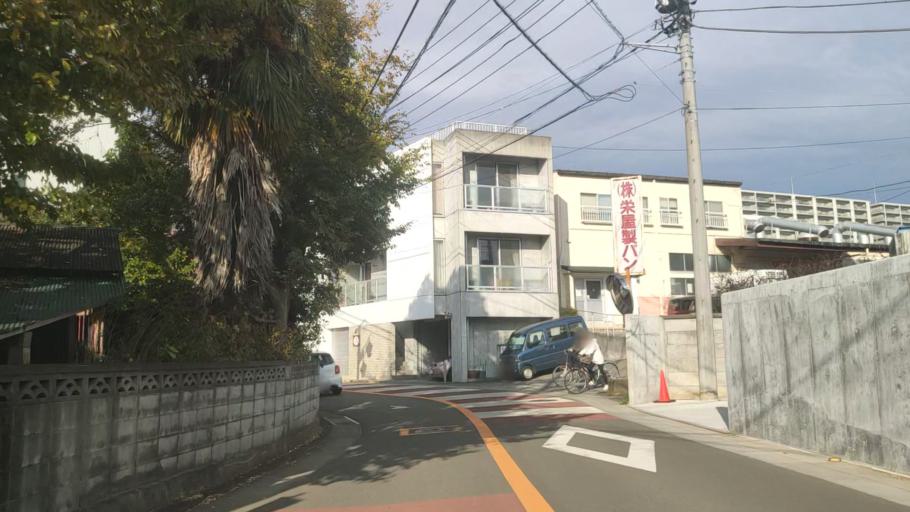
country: JP
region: Kanagawa
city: Zama
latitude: 35.4556
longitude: 139.3987
